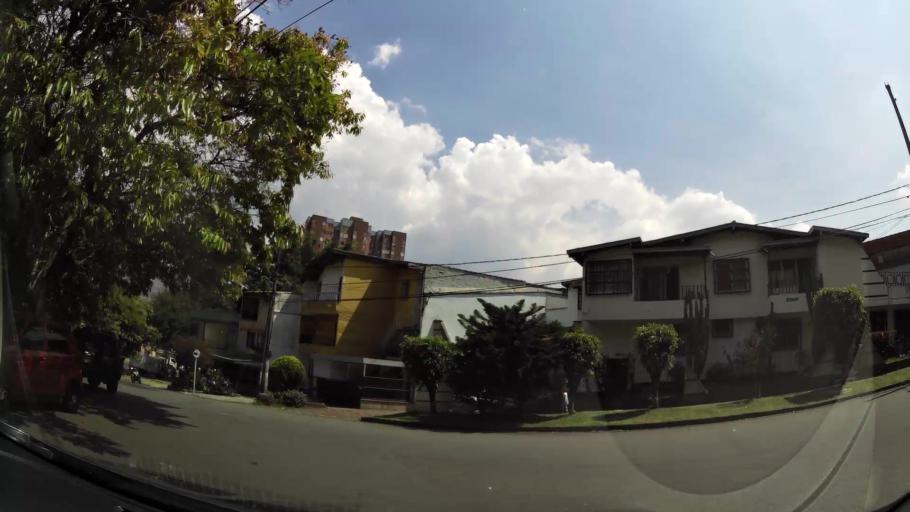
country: CO
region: Antioquia
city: Medellin
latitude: 6.2749
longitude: -75.5794
